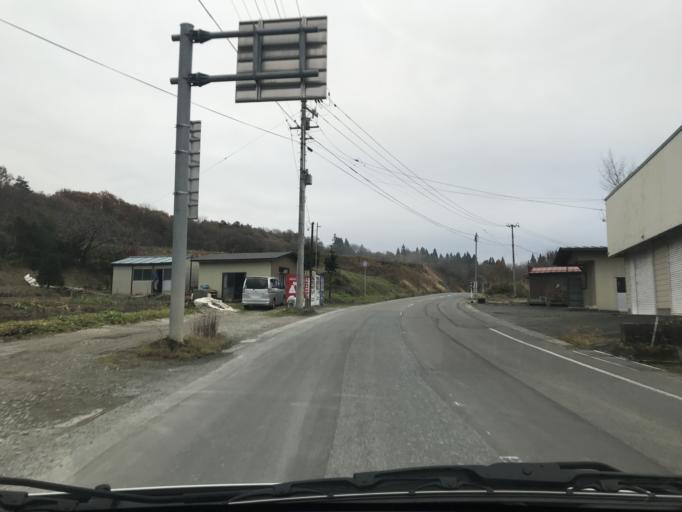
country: JP
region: Iwate
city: Kitakami
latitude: 39.2552
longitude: 141.2675
